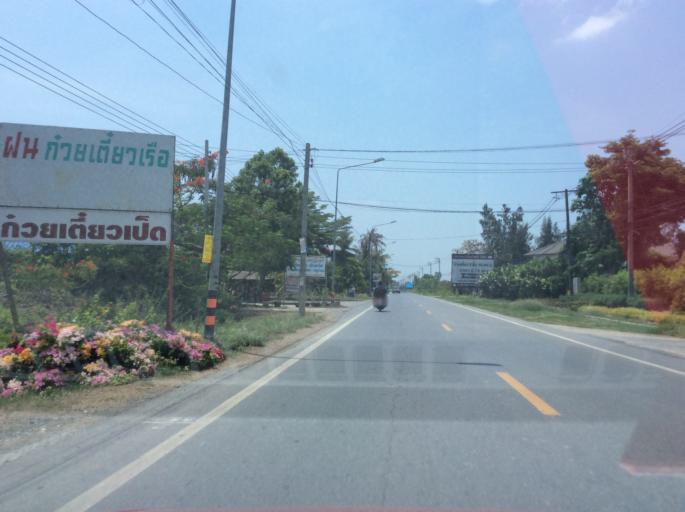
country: TH
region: Pathum Thani
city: Ban Rangsit
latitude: 14.0129
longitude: 100.7794
